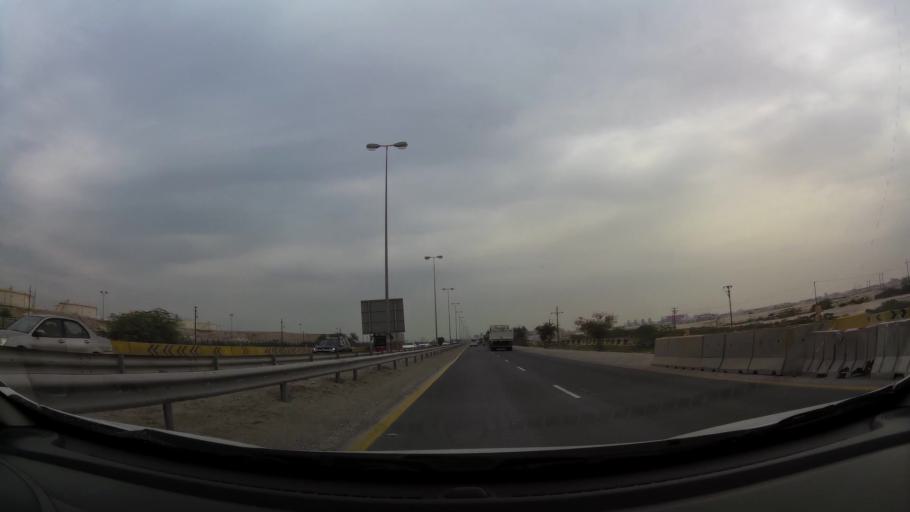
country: BH
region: Northern
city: Ar Rifa'
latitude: 26.1124
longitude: 50.5967
